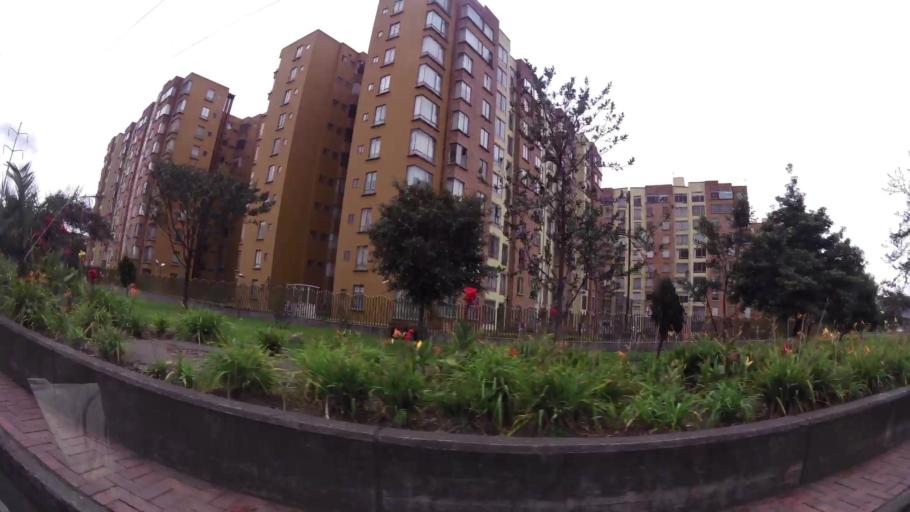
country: CO
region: Bogota D.C.
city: Bogota
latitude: 4.6492
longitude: -74.1071
